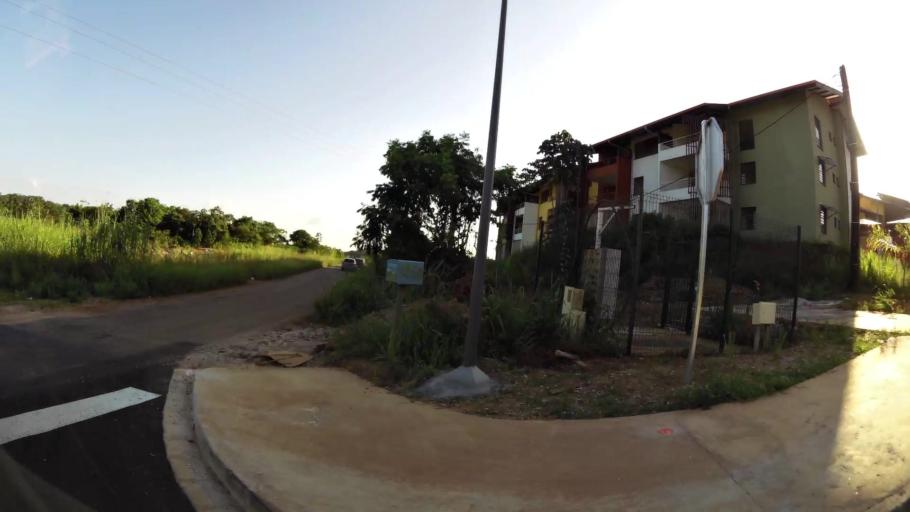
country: GF
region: Guyane
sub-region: Guyane
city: Remire-Montjoly
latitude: 4.8856
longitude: -52.2966
